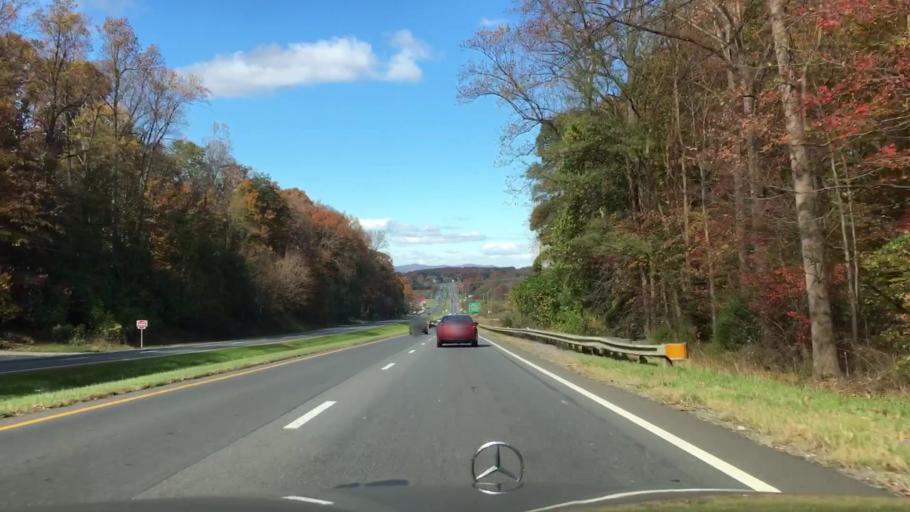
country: US
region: Virginia
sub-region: Campbell County
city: Rustburg
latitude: 37.3023
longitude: -79.1758
